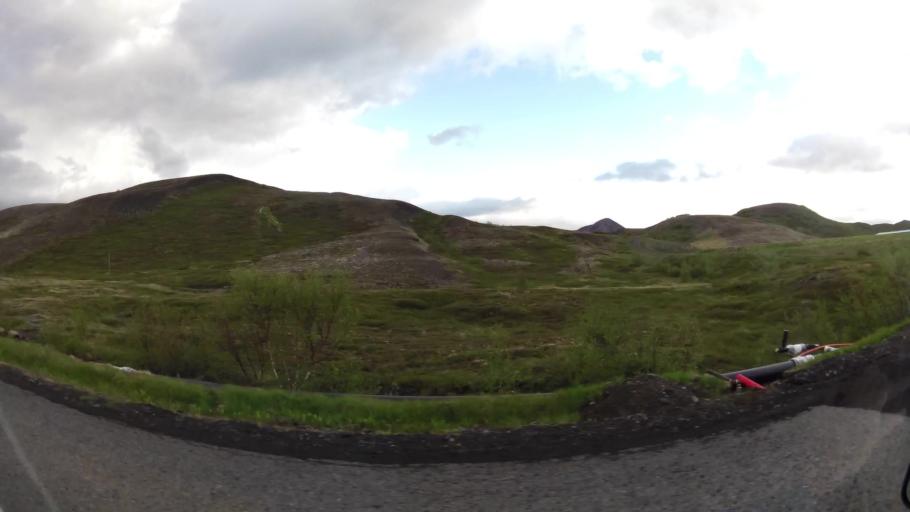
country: IS
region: Northeast
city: Laugar
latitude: 65.6422
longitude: -16.8992
